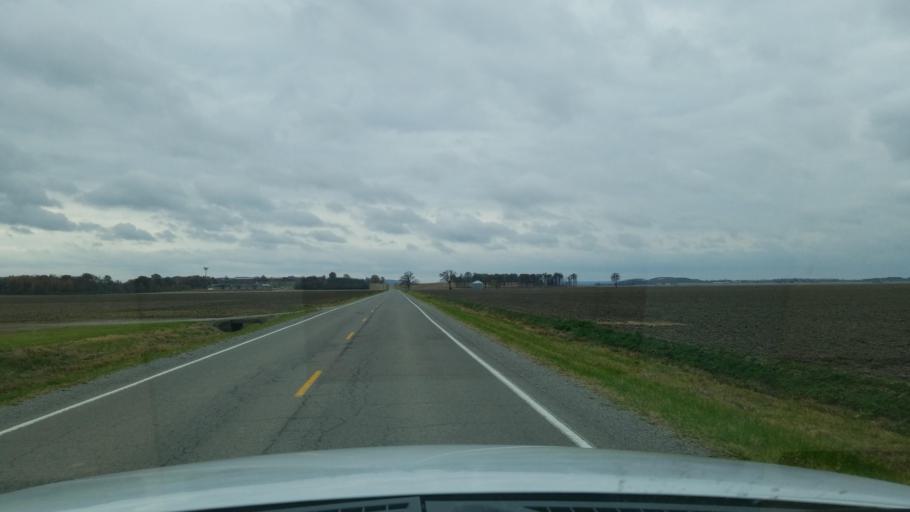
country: US
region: Illinois
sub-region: Saline County
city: Eldorado
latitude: 37.7669
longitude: -88.4382
